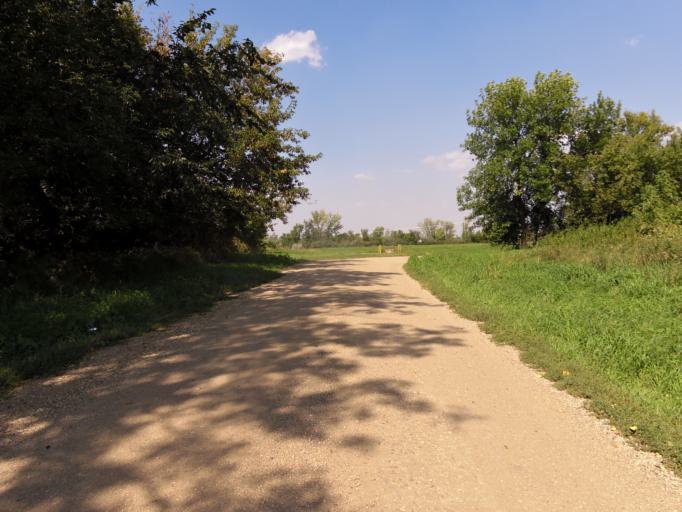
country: US
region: North Dakota
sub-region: Walsh County
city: Grafton
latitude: 48.4265
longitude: -97.4010
